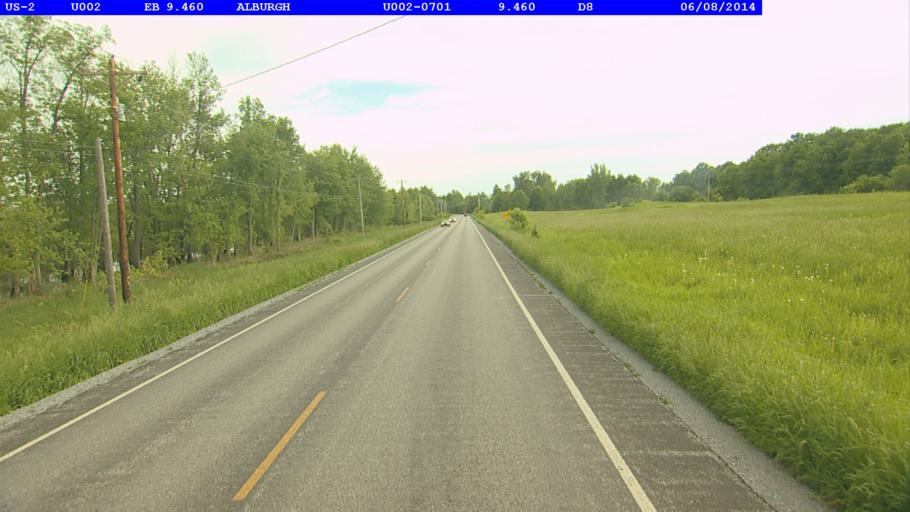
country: US
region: Vermont
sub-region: Grand Isle County
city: North Hero
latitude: 44.9146
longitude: -73.2780
